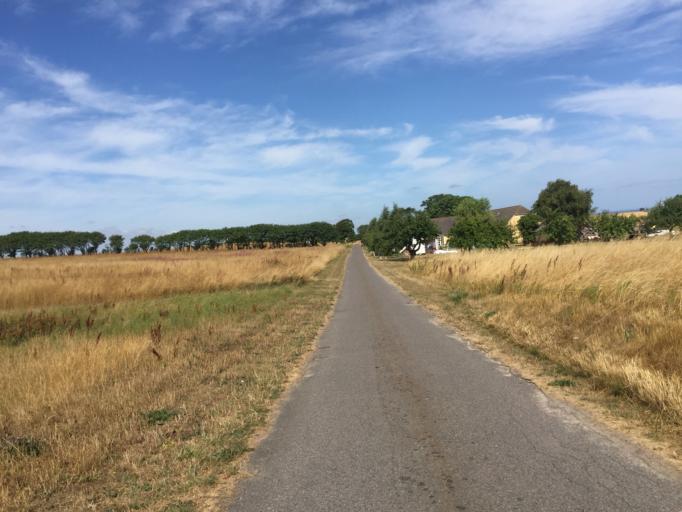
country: DK
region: Central Jutland
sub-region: Samso Kommune
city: Tranebjerg
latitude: 55.9532
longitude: 10.4251
